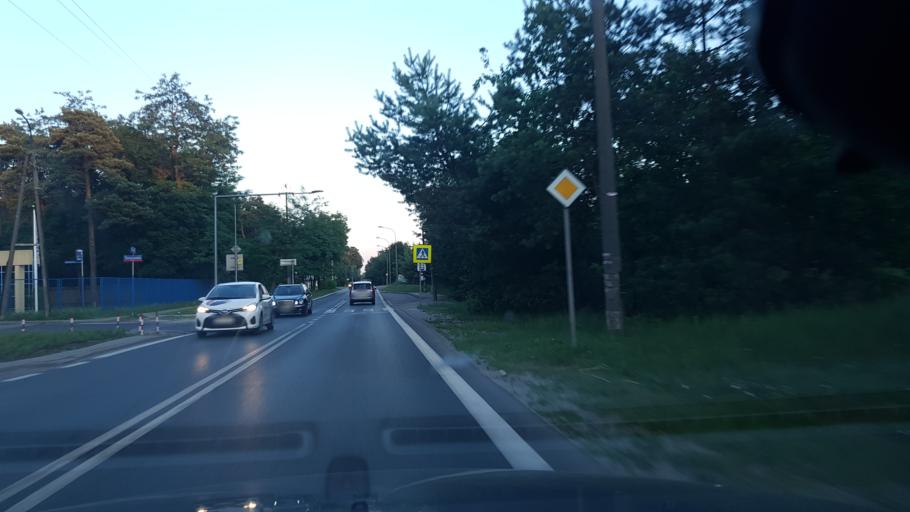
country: PL
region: Masovian Voivodeship
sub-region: Warszawa
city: Wawer
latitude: 52.1819
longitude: 21.1916
